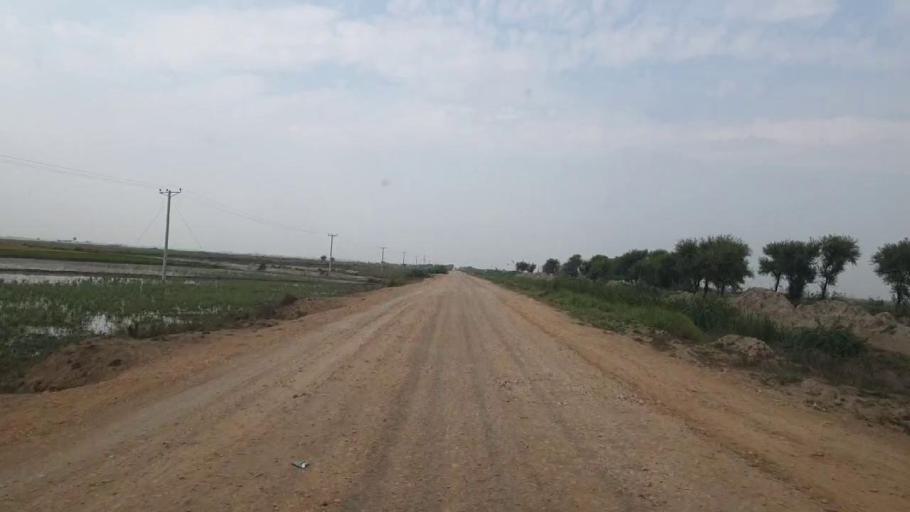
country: PK
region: Sindh
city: Kario
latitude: 24.6133
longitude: 68.5897
